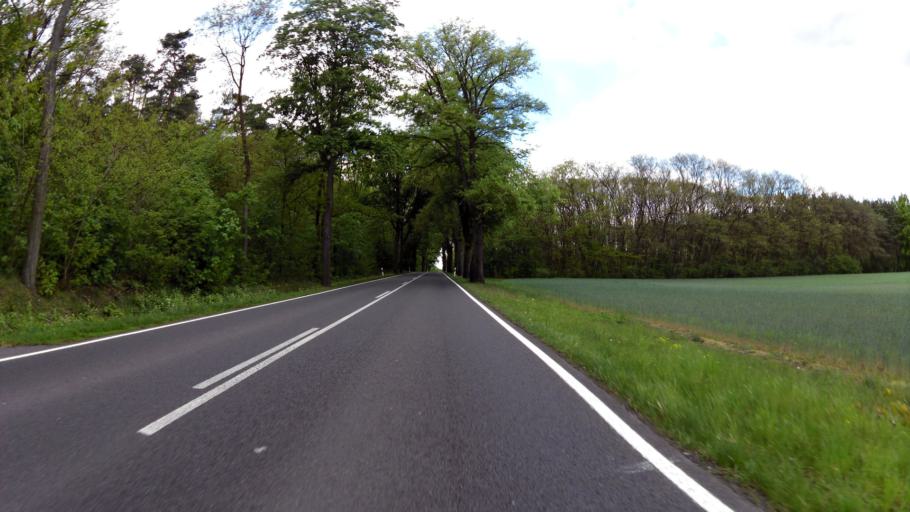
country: DE
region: Brandenburg
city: Langewahl
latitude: 52.3132
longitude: 14.1213
